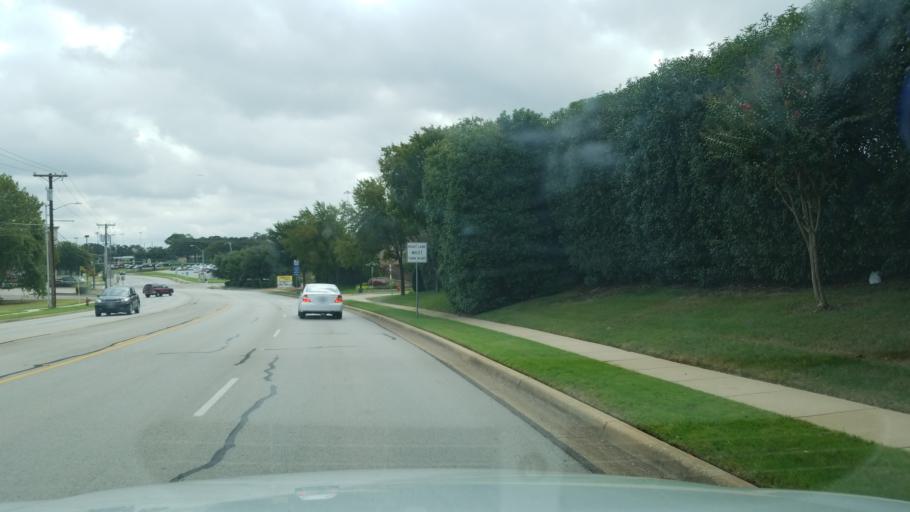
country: US
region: Texas
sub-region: Tarrant County
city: Euless
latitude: 32.8443
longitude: -97.1022
